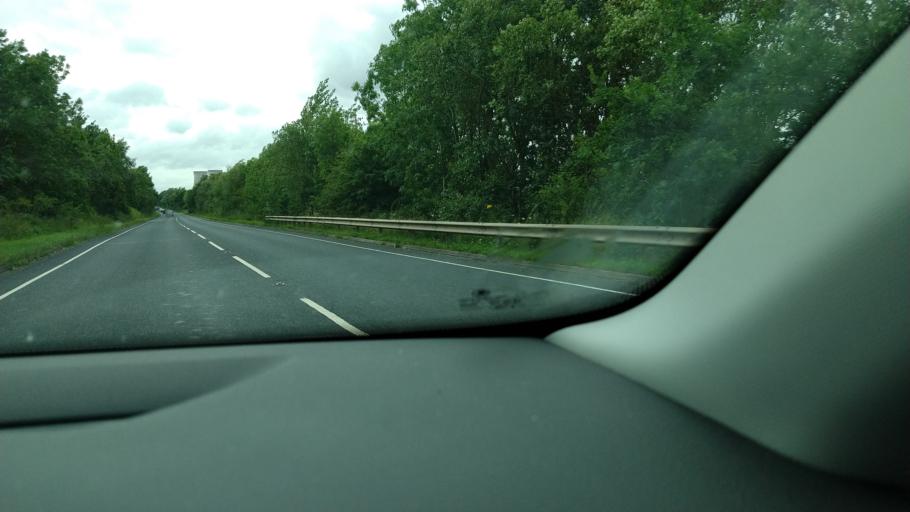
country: GB
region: England
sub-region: East Riding of Yorkshire
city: Barmby on the Marsh
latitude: 53.7155
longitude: -0.9616
